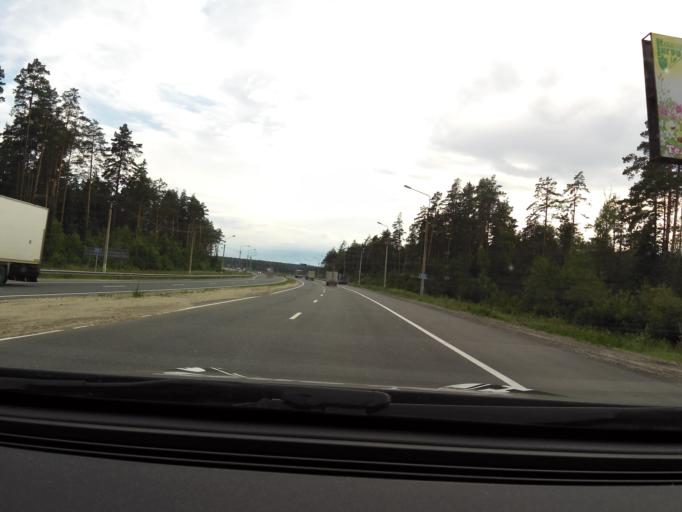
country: RU
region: Vladimir
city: Kommunar
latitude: 56.0848
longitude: 40.4815
